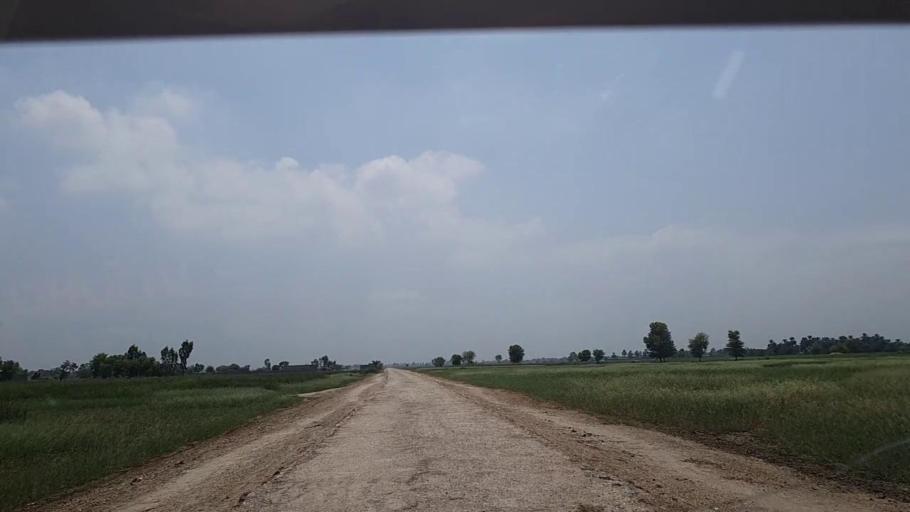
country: PK
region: Sindh
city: Khanpur
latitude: 27.9067
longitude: 69.3922
